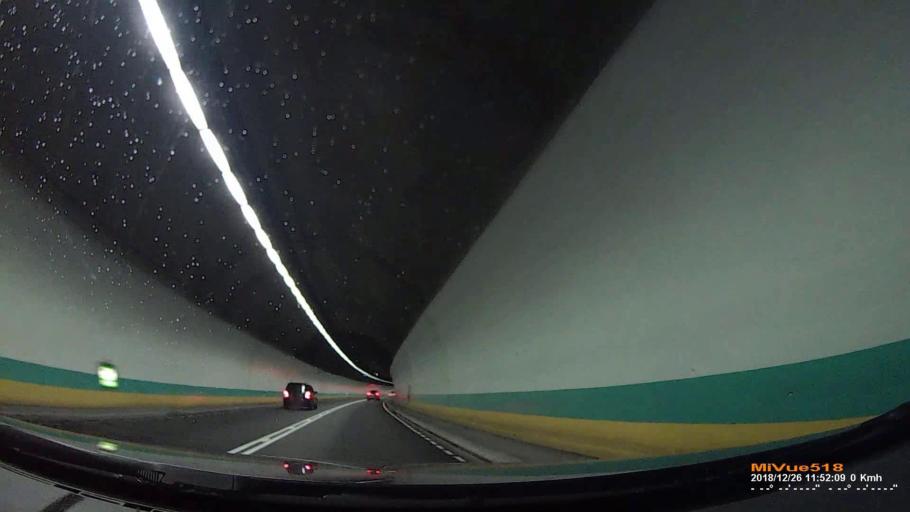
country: TW
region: Taiwan
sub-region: Keelung
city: Keelung
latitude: 24.9691
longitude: 121.6825
